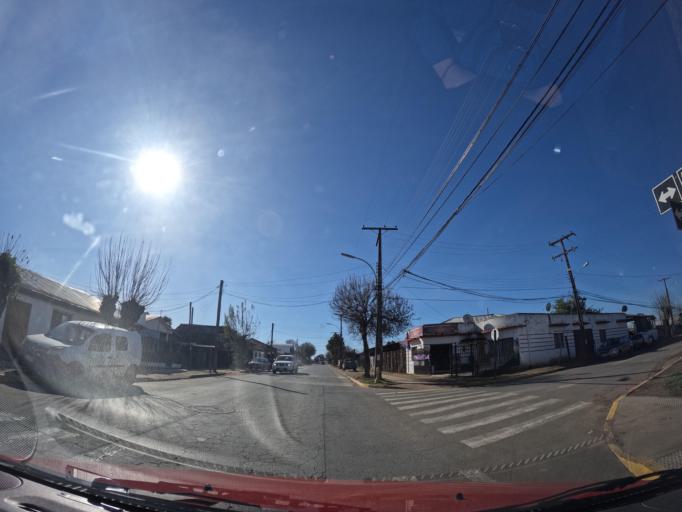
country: CL
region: Maule
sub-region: Provincia de Cauquenes
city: Cauquenes
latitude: -35.9842
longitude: -72.3177
